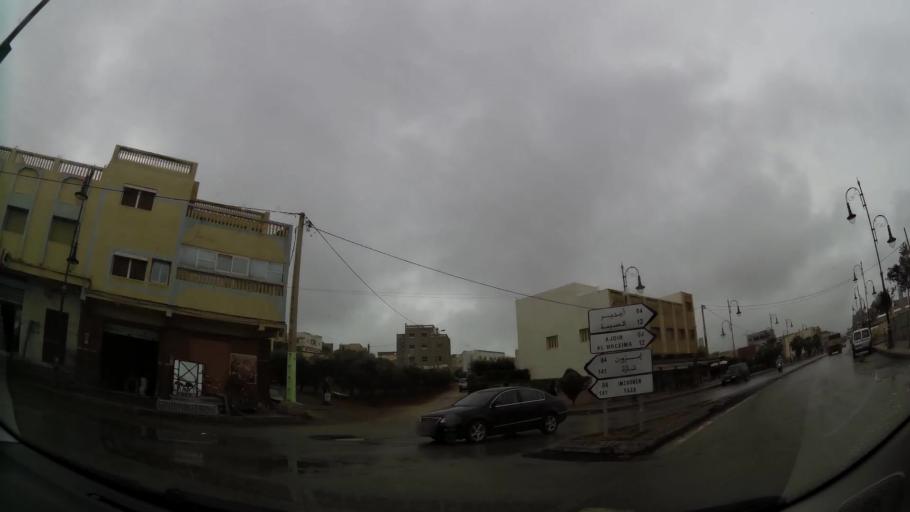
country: MA
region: Taza-Al Hoceima-Taounate
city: Imzourene
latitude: 35.1716
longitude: -3.8625
